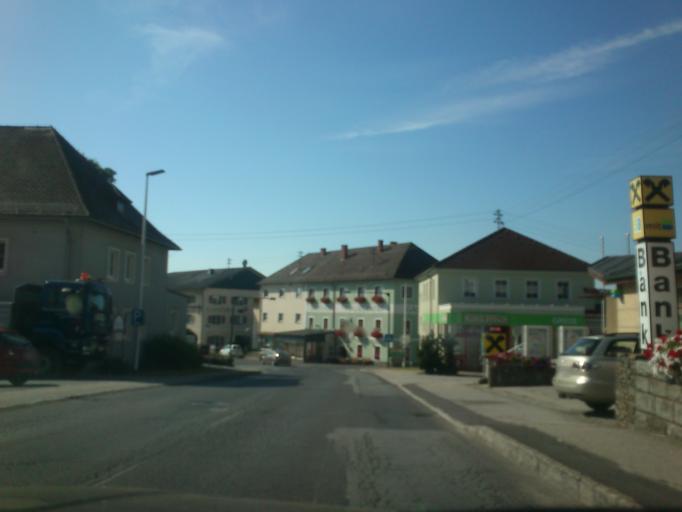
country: AT
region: Upper Austria
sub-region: Politischer Bezirk Freistadt
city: Freistadt
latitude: 48.5588
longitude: 14.4767
